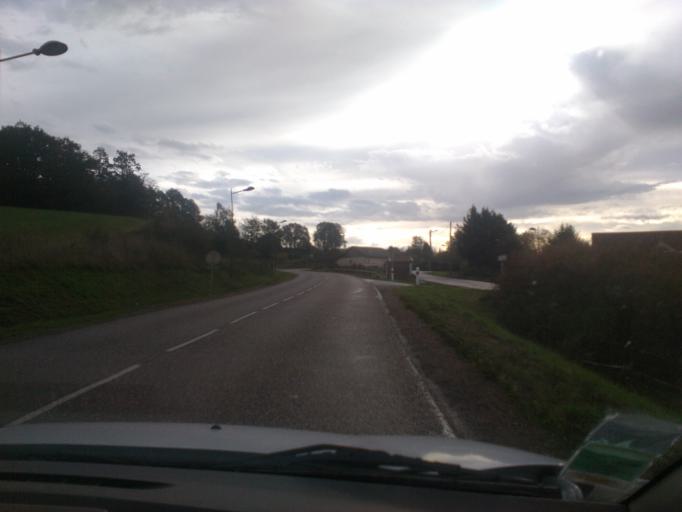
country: FR
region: Lorraine
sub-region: Departement des Vosges
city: Granges-sur-Vologne
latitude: 48.1764
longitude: 6.8303
